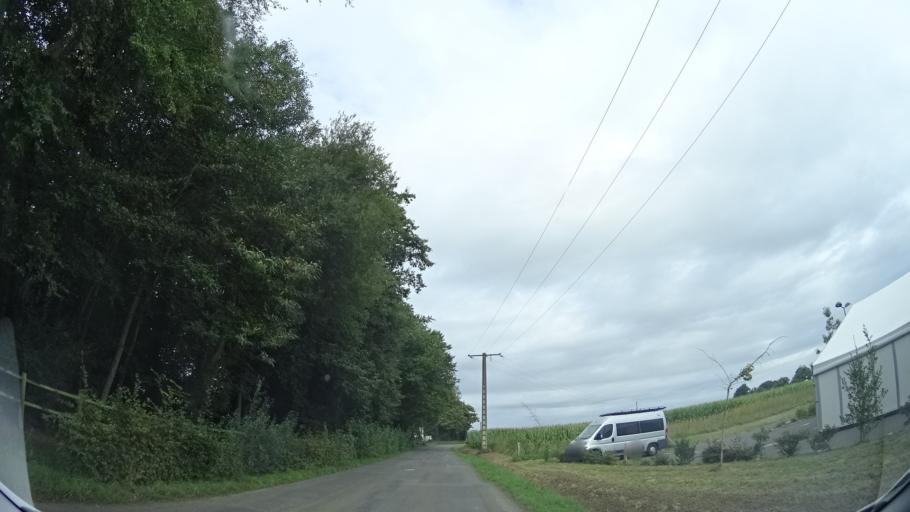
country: FR
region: Brittany
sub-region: Departement d'Ille-et-Vilaine
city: Hede-Bazouges
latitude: 48.2872
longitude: -1.8053
